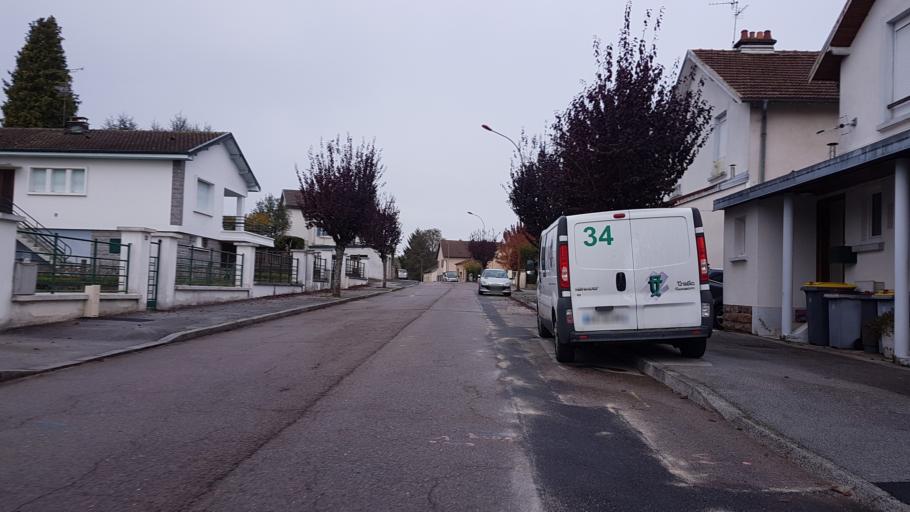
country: FR
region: Franche-Comte
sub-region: Departement de la Haute-Saone
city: Luxeuil-les-Bains
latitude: 47.8226
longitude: 6.3713
